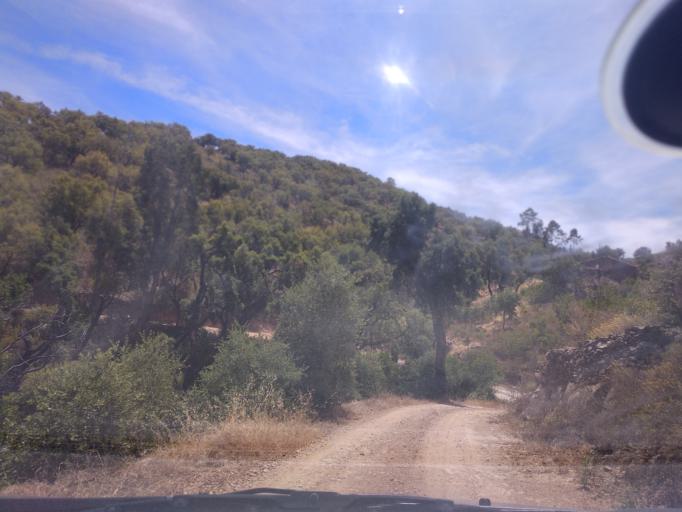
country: PT
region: Faro
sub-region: Sao Bras de Alportel
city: Sao Bras de Alportel
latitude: 37.2066
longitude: -7.8162
